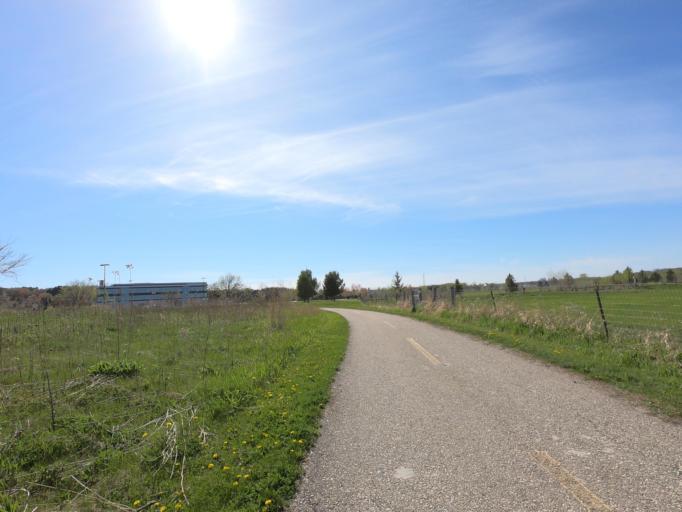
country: US
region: Wisconsin
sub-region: Dane County
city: Middleton
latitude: 43.1116
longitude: -89.5368
